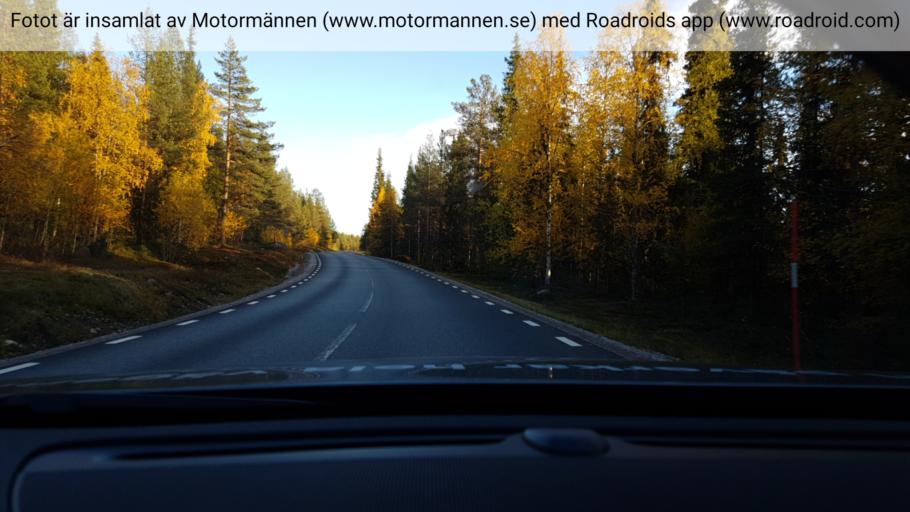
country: SE
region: Norrbotten
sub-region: Jokkmokks Kommun
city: Jokkmokk
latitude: 66.9409
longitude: 19.8044
